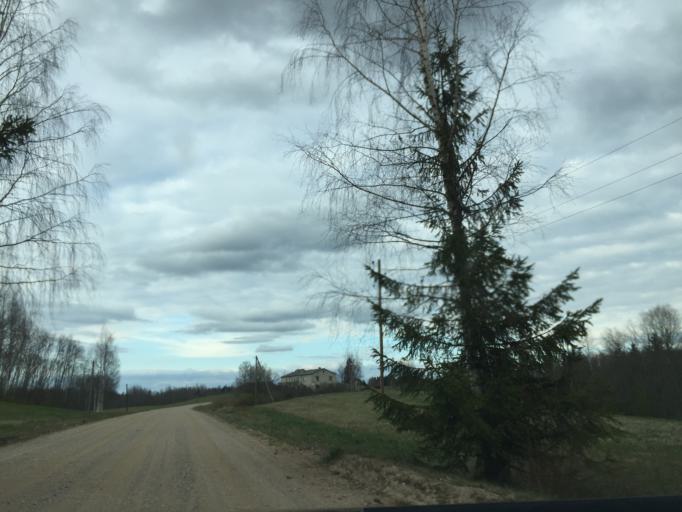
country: LV
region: Aluksnes Rajons
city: Aluksne
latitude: 57.4115
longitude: 27.0043
